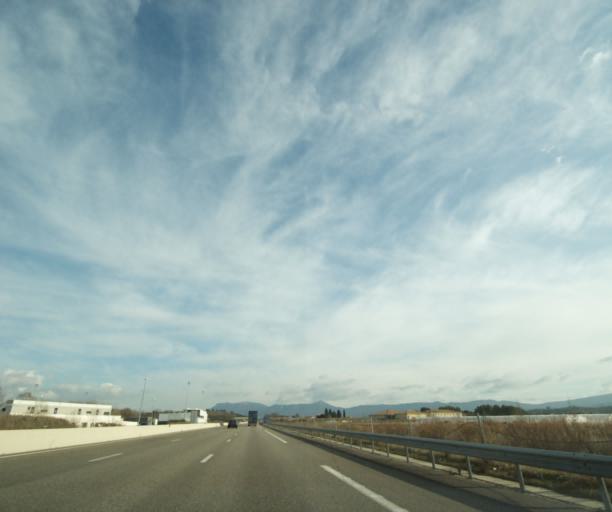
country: FR
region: Provence-Alpes-Cote d'Azur
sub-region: Departement des Bouches-du-Rhone
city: Rousset
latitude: 43.4763
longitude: 5.6204
